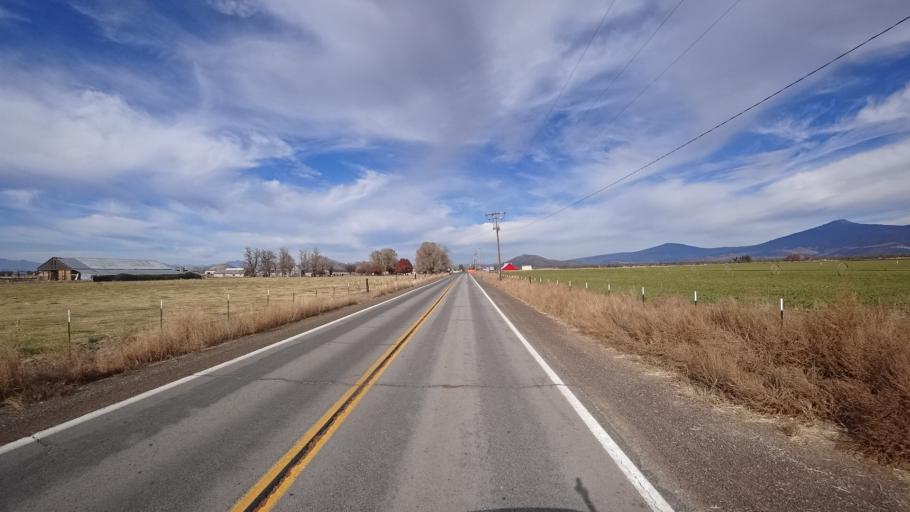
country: US
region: California
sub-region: Siskiyou County
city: Montague
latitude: 41.6168
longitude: -122.3997
